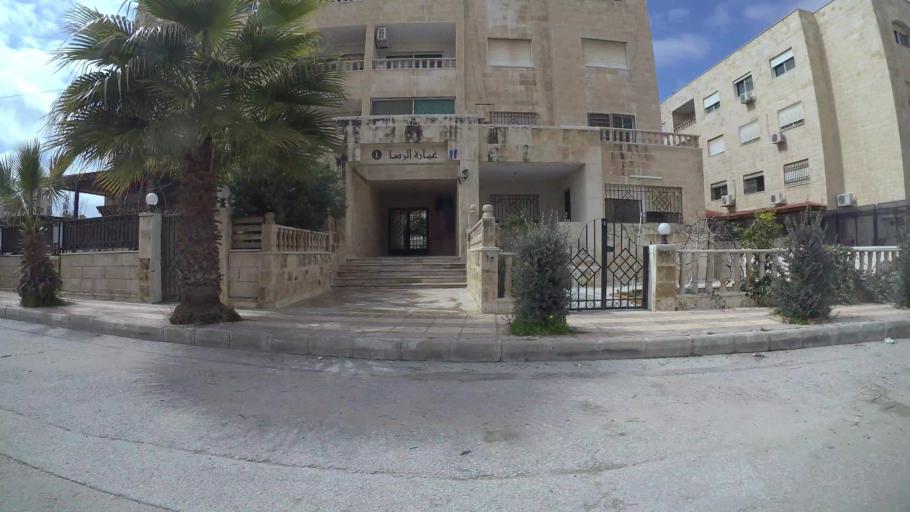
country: JO
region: Amman
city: Al Jubayhah
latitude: 31.9923
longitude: 35.8474
